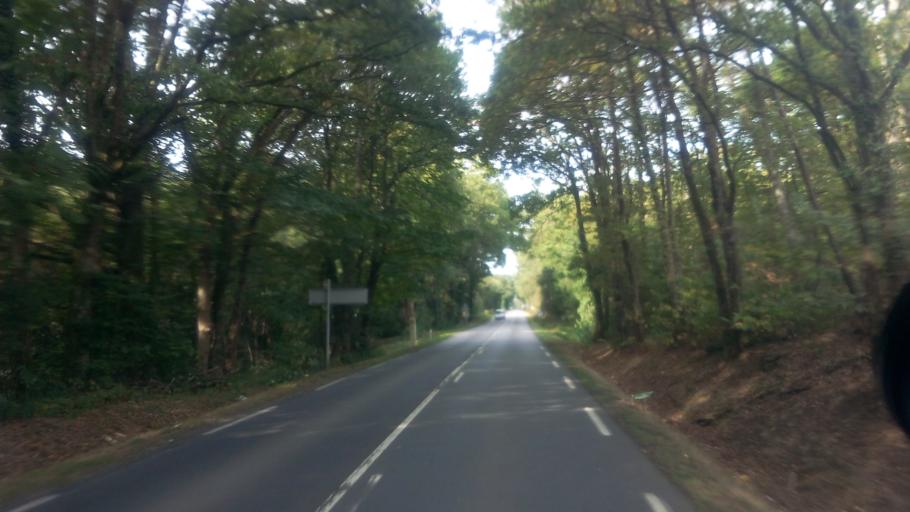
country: FR
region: Brittany
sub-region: Departement du Morbihan
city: La Gacilly
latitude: 47.7364
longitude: -2.1080
